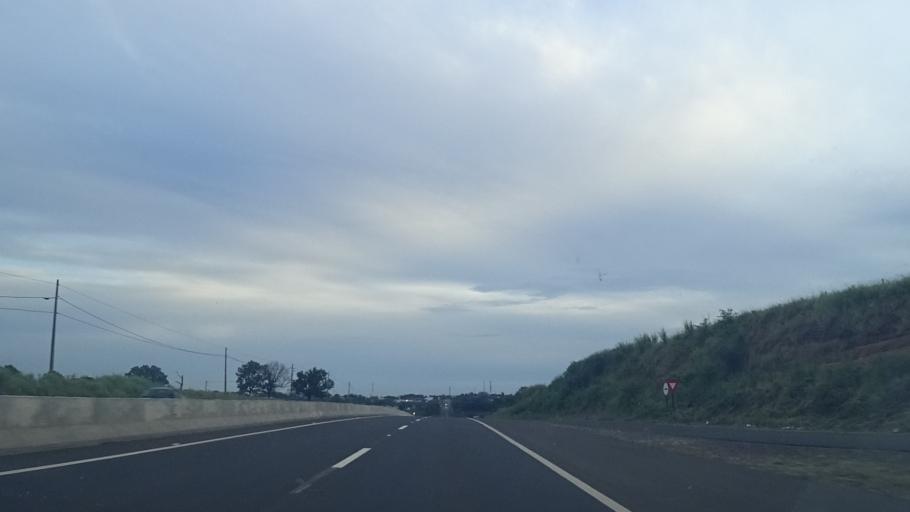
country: BR
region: Sao Paulo
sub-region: Presidente Prudente
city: Presidente Prudente
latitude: -22.1692
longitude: -51.4005
